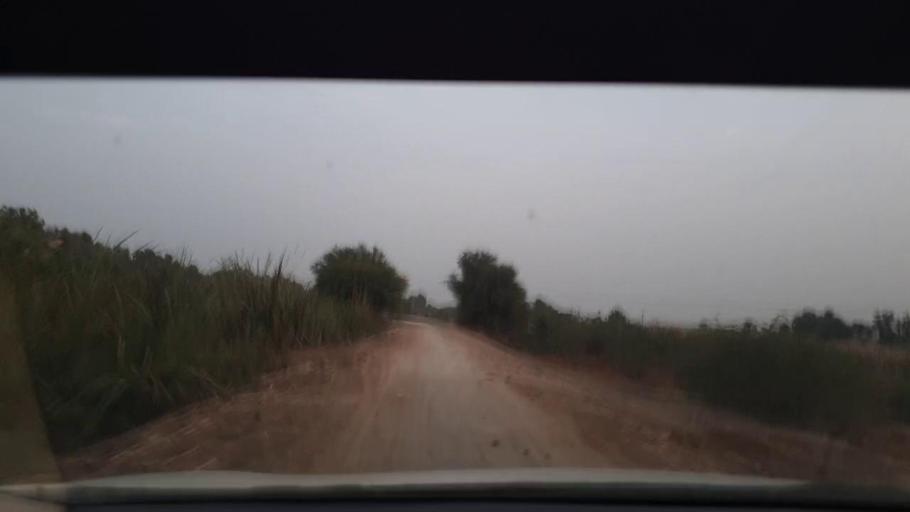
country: PK
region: Sindh
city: Berani
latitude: 25.8461
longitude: 68.7868
